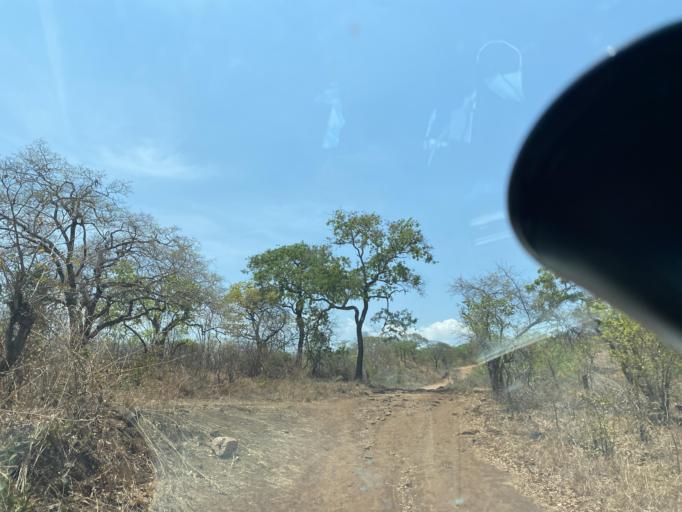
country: ZM
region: Lusaka
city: Kafue
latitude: -15.8073
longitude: 28.4389
